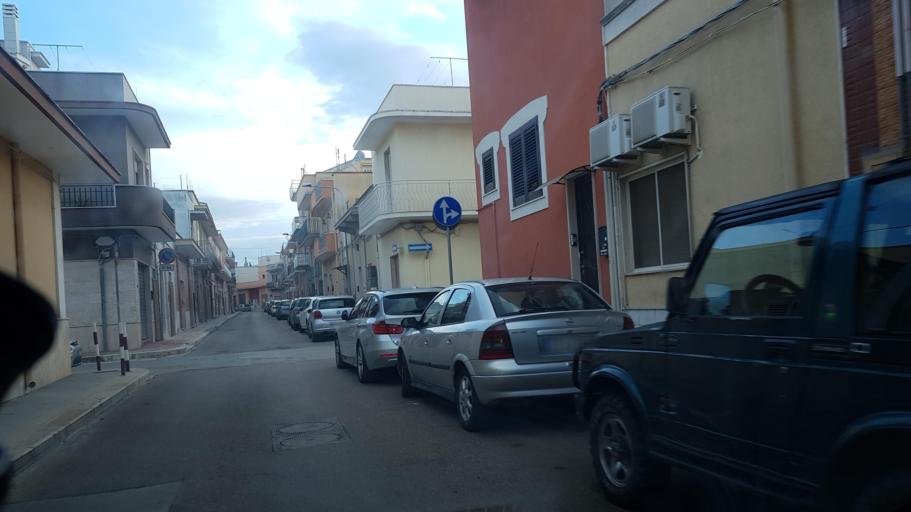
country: IT
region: Apulia
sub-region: Provincia di Brindisi
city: San Vito dei Normanni
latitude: 40.6556
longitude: 17.6989
